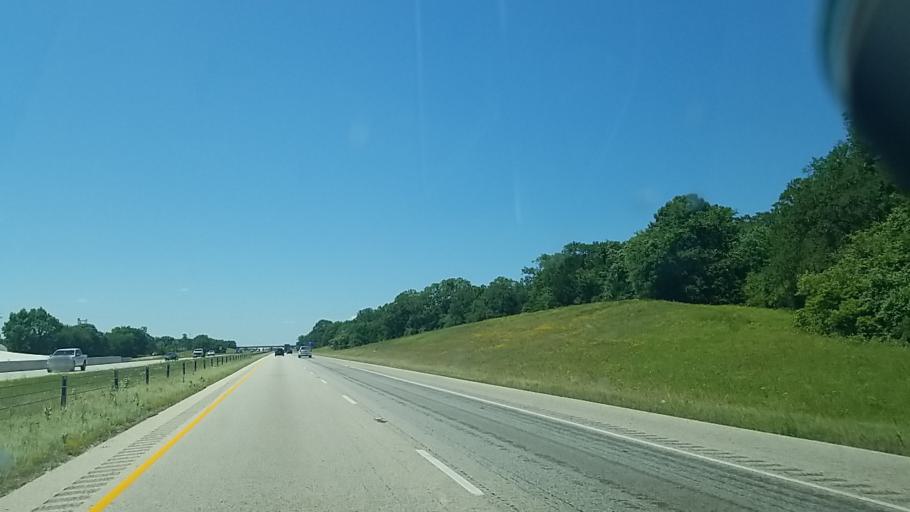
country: US
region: Texas
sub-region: Leon County
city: Buffalo
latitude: 31.4379
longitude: -96.0641
